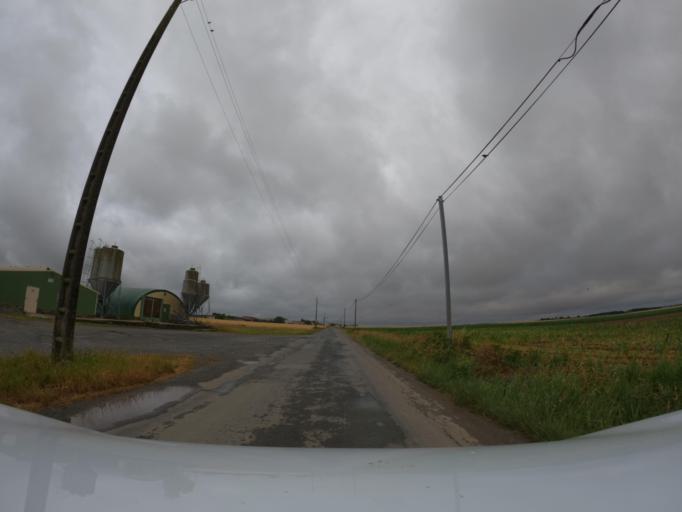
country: FR
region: Pays de la Loire
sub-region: Departement de la Vendee
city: Maillezais
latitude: 46.4046
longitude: -0.7276
